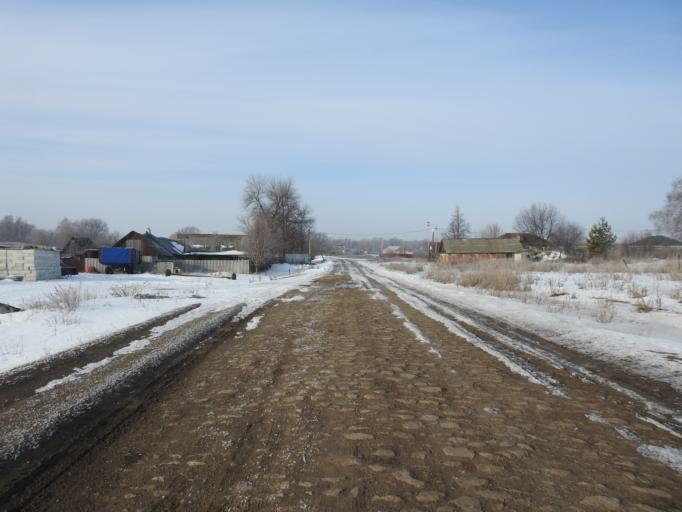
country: RU
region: Saratov
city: Krasnyy Oktyabr'
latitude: 51.4924
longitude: 45.7270
